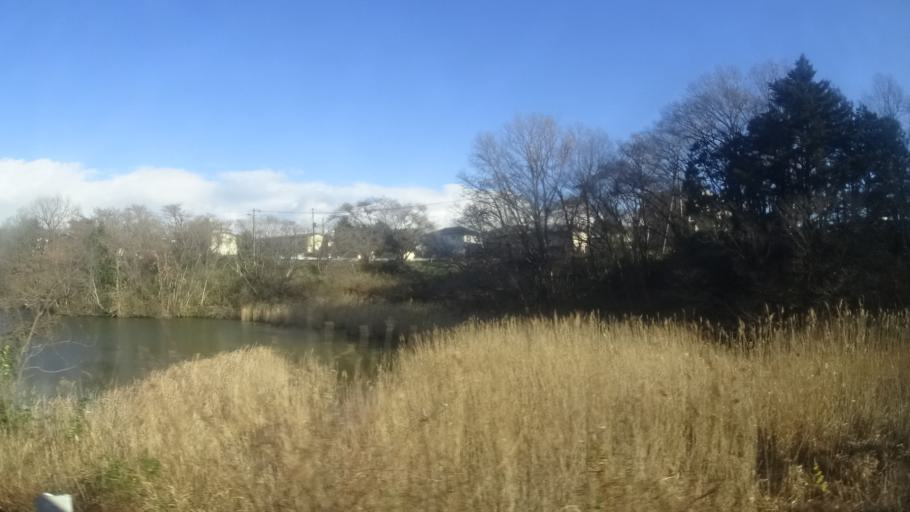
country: JP
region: Miyagi
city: Marumori
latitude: 37.8126
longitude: 140.9231
